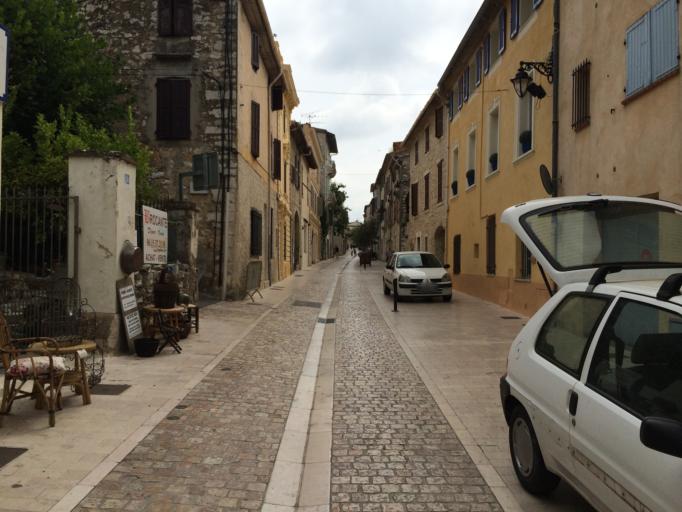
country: FR
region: Provence-Alpes-Cote d'Azur
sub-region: Departement des Alpes-Maritimes
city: La Colle-sur-Loup
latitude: 43.6871
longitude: 7.1007
